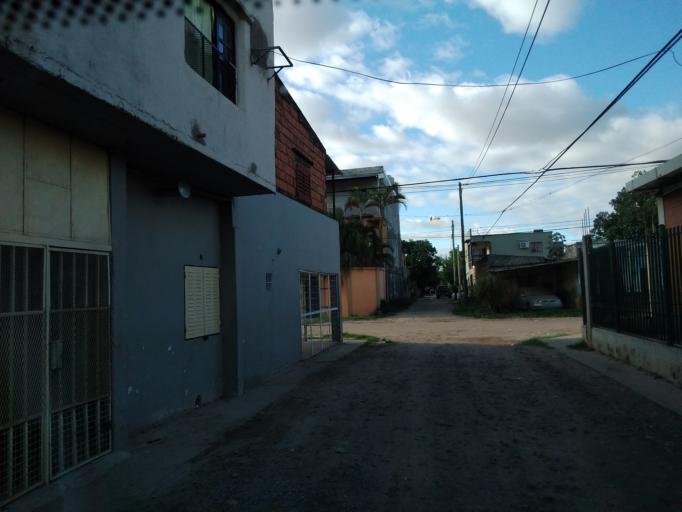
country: AR
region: Corrientes
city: Corrientes
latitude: -27.4783
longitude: -58.8085
